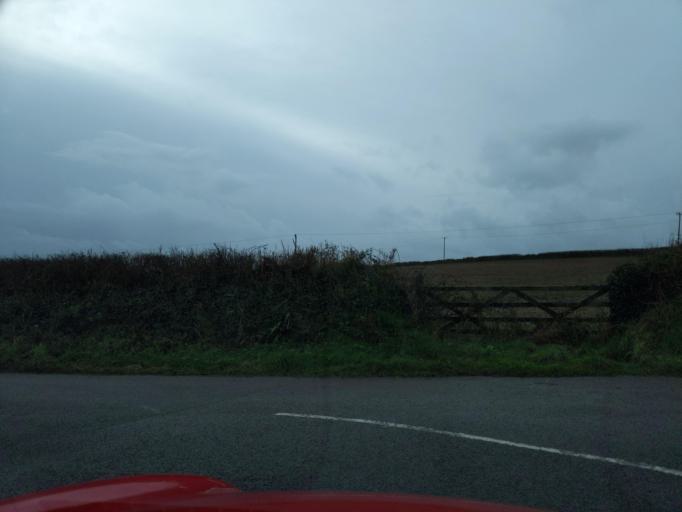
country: GB
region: England
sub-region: Cornwall
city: Duloe
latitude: 50.3565
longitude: -4.5168
